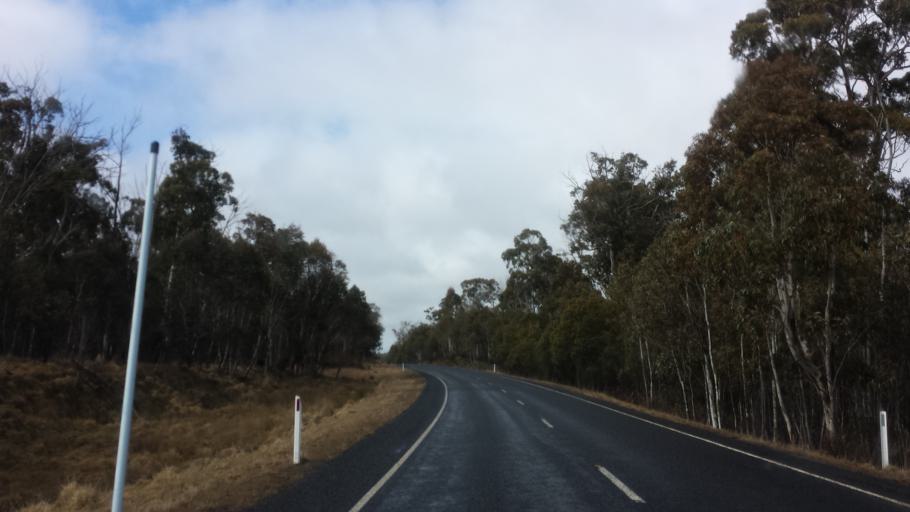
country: AU
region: Victoria
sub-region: Alpine
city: Mount Beauty
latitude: -37.0679
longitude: 147.3431
